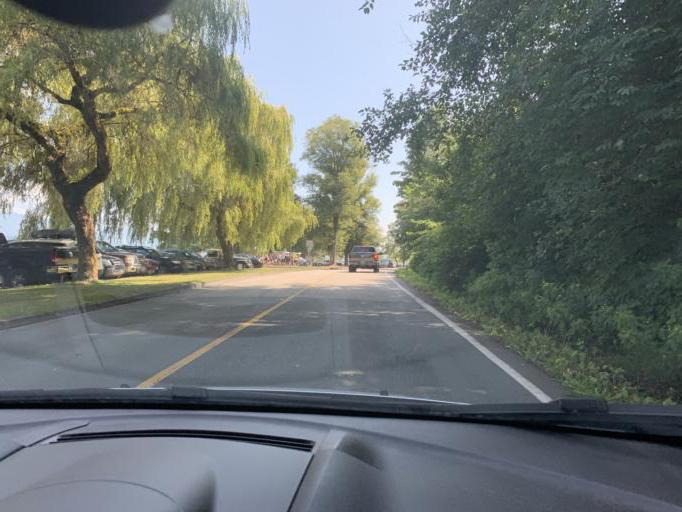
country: CA
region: British Columbia
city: West End
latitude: 49.2774
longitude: -123.2240
